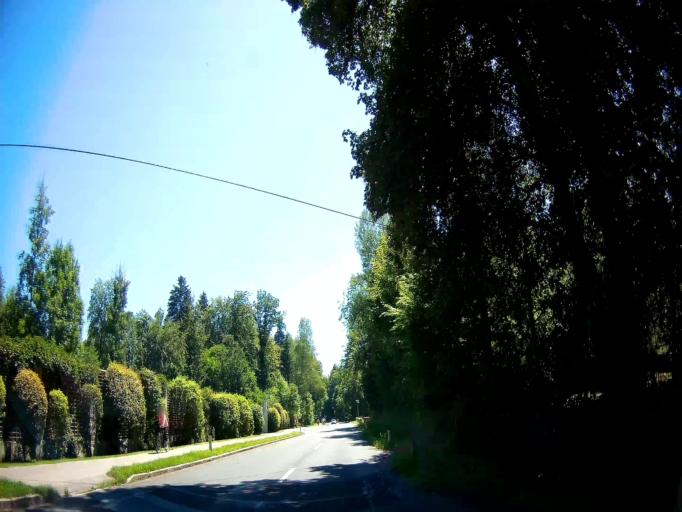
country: AT
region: Carinthia
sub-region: Politischer Bezirk Klagenfurt Land
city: Kottmannsdorf
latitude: 46.6087
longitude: 14.2490
